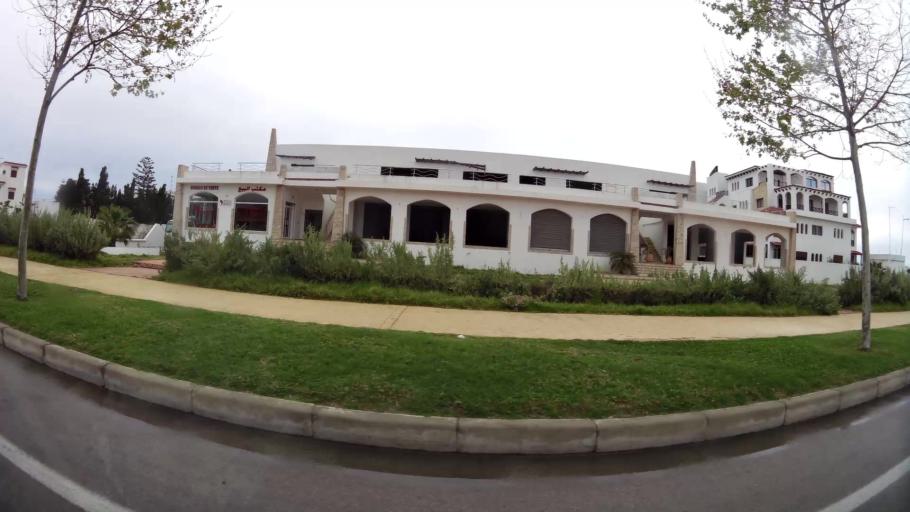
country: MA
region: Tanger-Tetouan
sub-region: Tetouan
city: Martil
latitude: 35.6328
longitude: -5.2859
